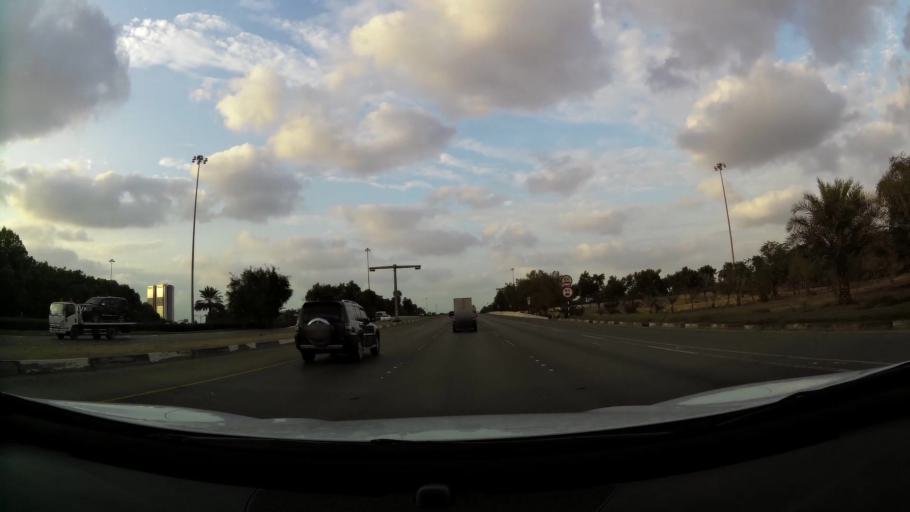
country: AE
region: Abu Dhabi
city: Abu Dhabi
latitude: 24.3896
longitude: 54.5241
